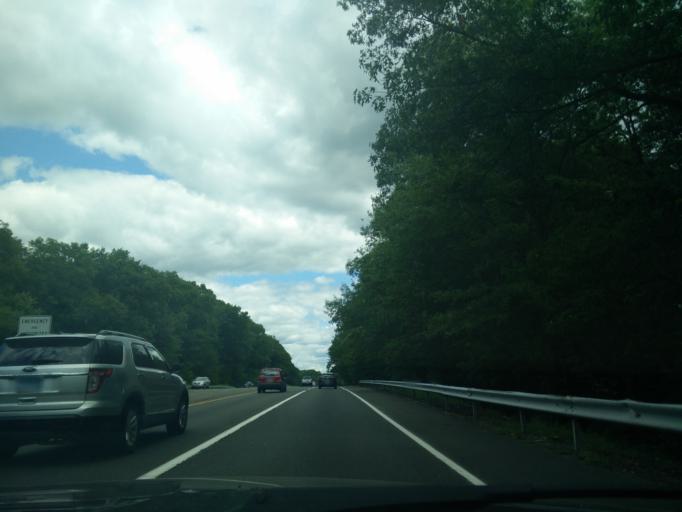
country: US
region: Connecticut
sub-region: New Haven County
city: Woodbridge
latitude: 41.3468
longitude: -72.9678
